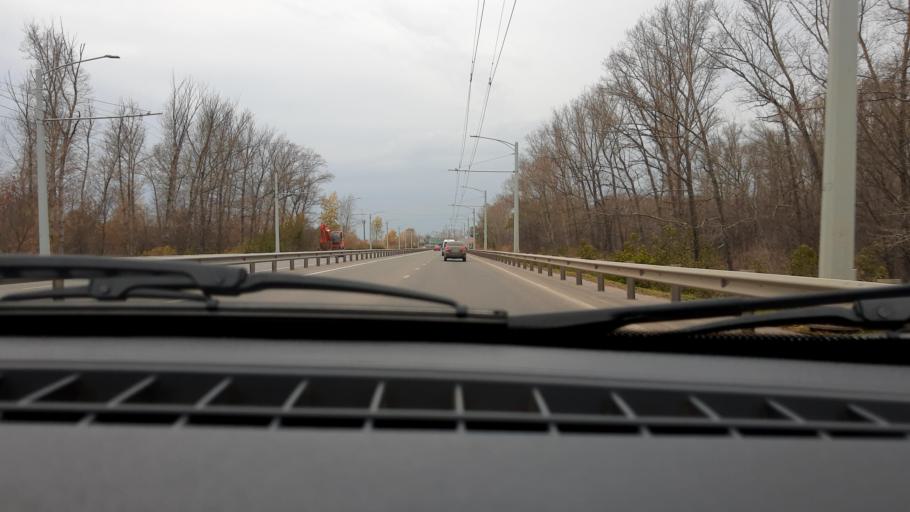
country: RU
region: Bashkortostan
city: Mikhaylovka
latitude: 54.7736
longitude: 55.8984
